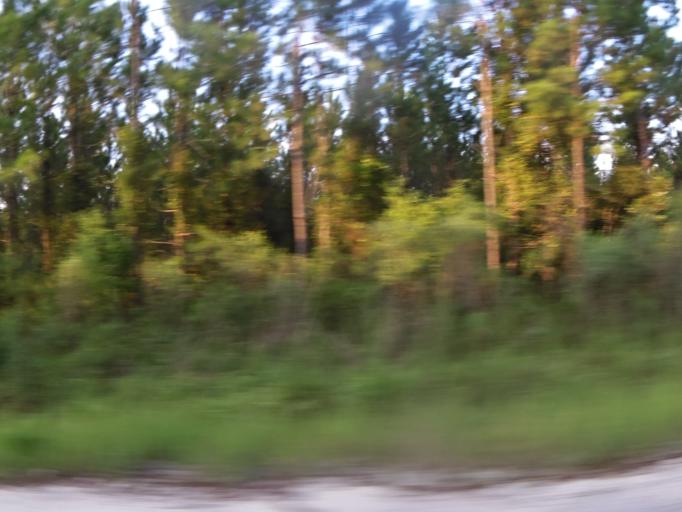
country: US
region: Florida
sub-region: Duval County
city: Baldwin
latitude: 30.3856
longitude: -82.0449
